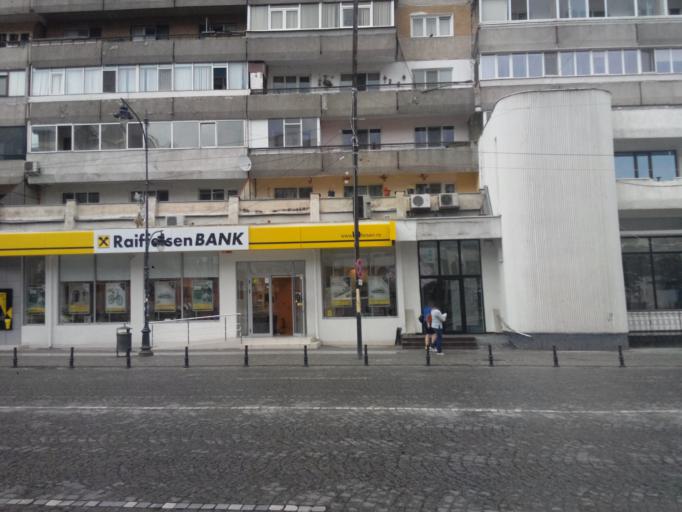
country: RO
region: Iasi
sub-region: Municipiul Iasi
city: Iasi
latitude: 47.1627
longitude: 27.5823
